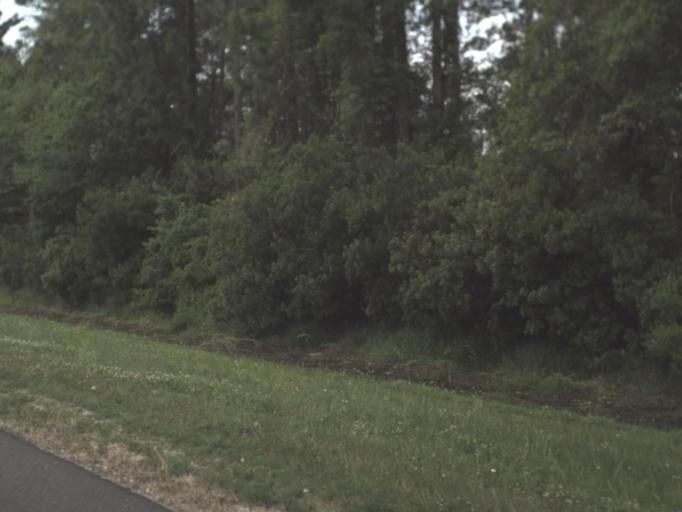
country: US
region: Florida
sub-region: Saint Johns County
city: Fruit Cove
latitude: 30.1004
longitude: -81.7059
